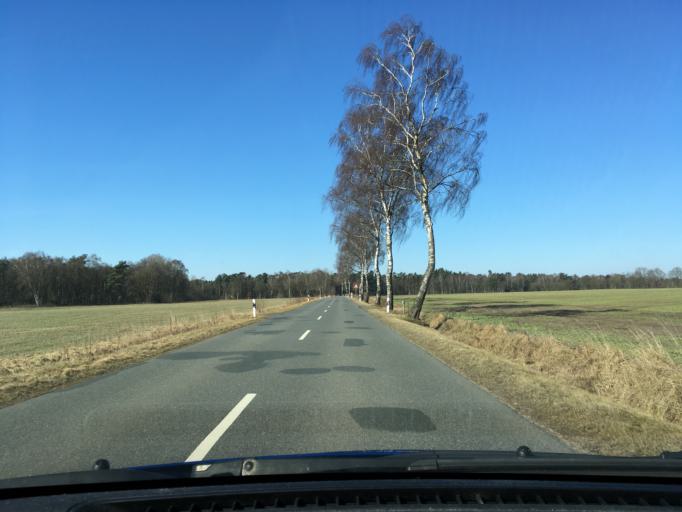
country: DE
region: Lower Saxony
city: Schneverdingen
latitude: 53.0827
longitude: 9.8446
